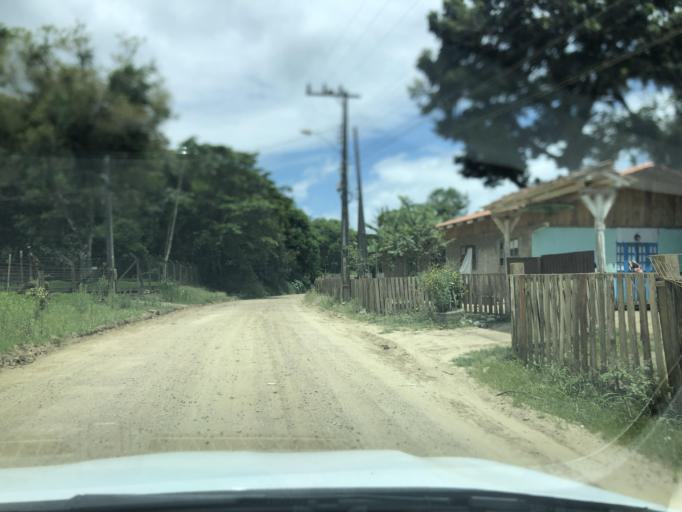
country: BR
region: Santa Catarina
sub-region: Sao Francisco Do Sul
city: Sao Francisco do Sul
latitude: -26.2284
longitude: -48.5867
